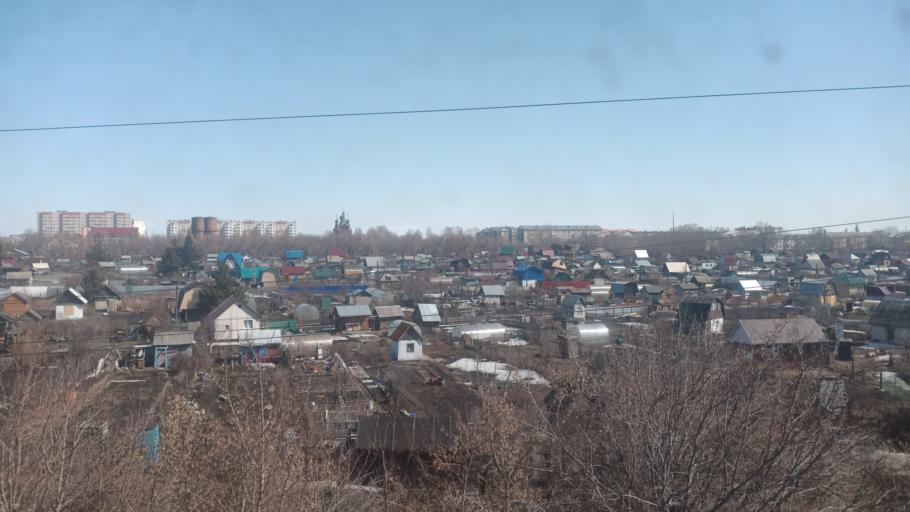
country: RU
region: Altai Krai
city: Beloyarsk
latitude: 53.4211
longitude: 83.9203
